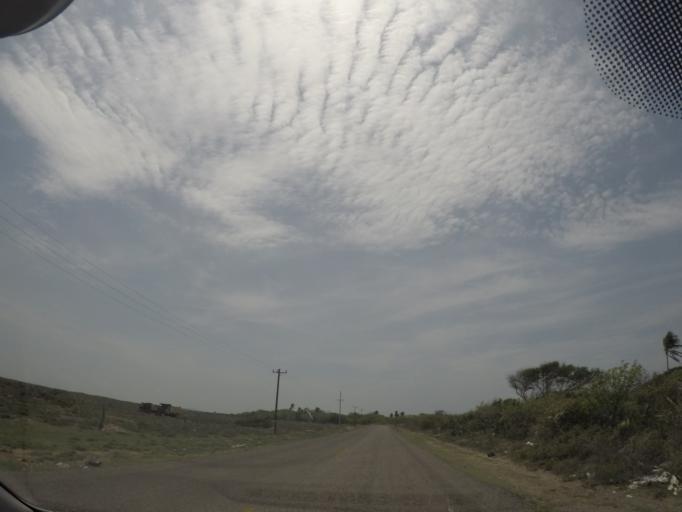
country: MX
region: Oaxaca
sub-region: San Mateo del Mar
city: Colonia Juarez
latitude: 16.2123
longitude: -95.0497
